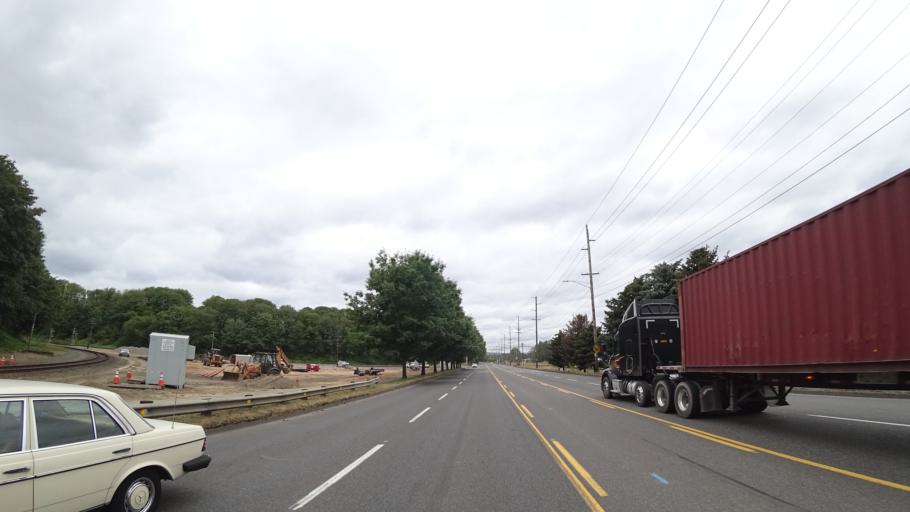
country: US
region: Washington
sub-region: Clark County
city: Vancouver
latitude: 45.5922
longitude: -122.7101
